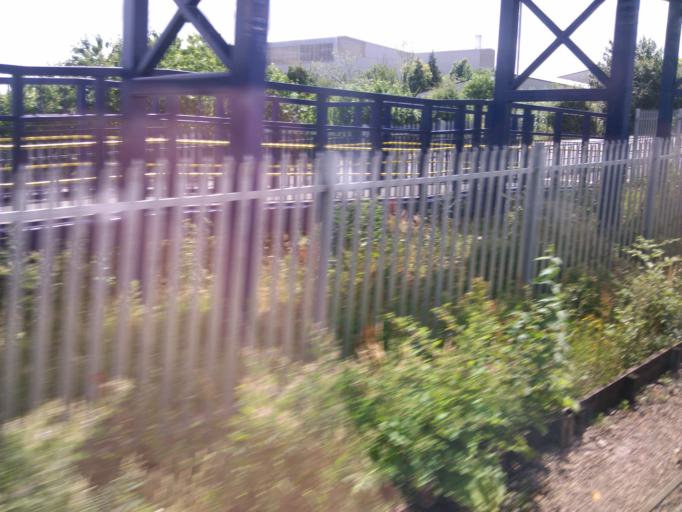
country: GB
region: England
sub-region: Essex
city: Witham
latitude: 51.8105
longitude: 0.6479
